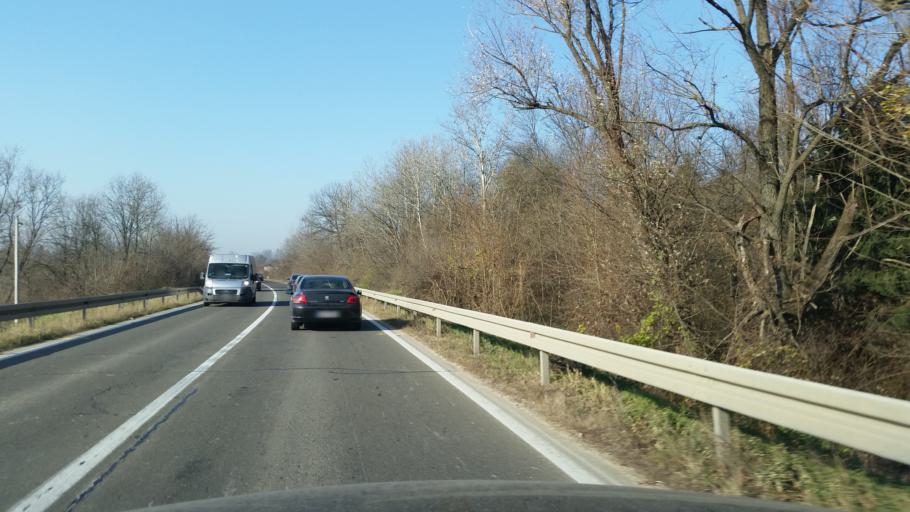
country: RS
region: Central Serbia
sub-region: Kolubarski Okrug
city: Ljig
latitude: 44.3055
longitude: 20.2563
